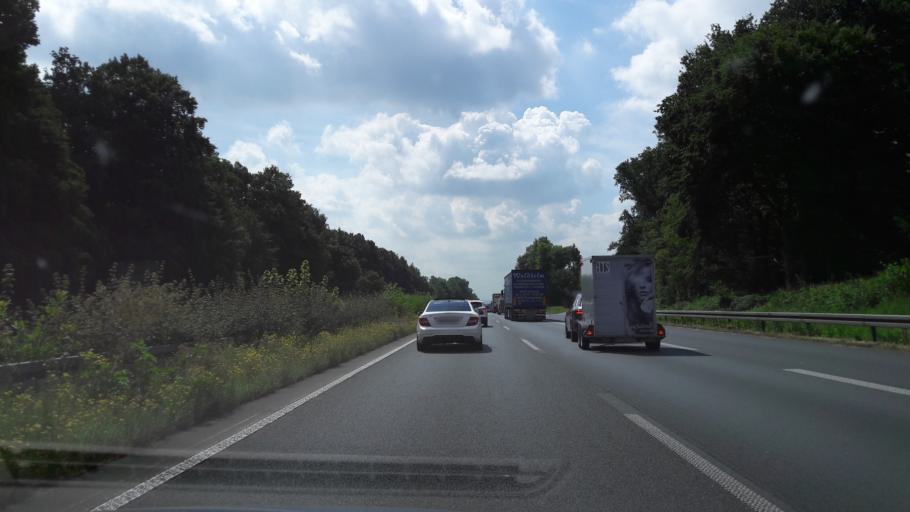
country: DE
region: North Rhine-Westphalia
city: Werne
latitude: 51.6761
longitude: 7.6795
